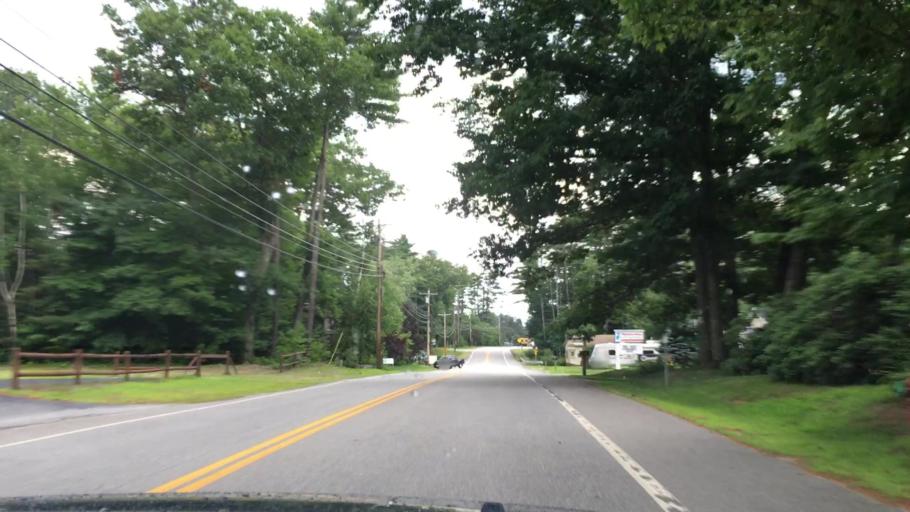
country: US
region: New Hampshire
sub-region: Belknap County
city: Meredith
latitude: 43.6728
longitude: -71.5047
